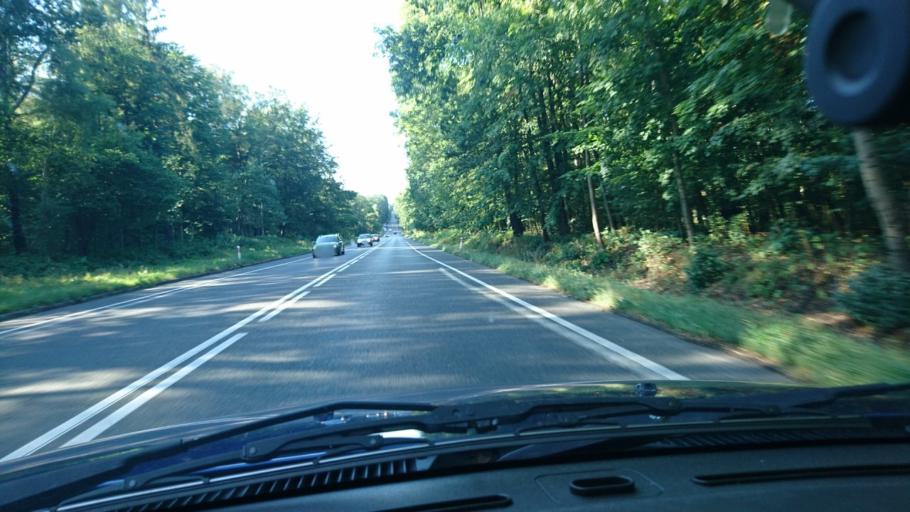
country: PL
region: Silesian Voivodeship
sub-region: Gliwice
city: Gliwice
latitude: 50.3260
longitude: 18.6608
